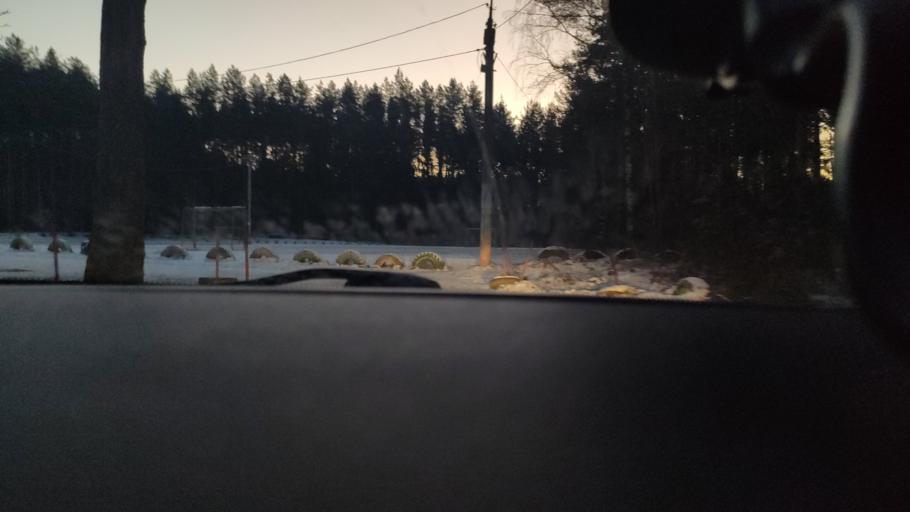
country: RU
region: Perm
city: Perm
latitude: 57.9945
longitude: 56.1824
